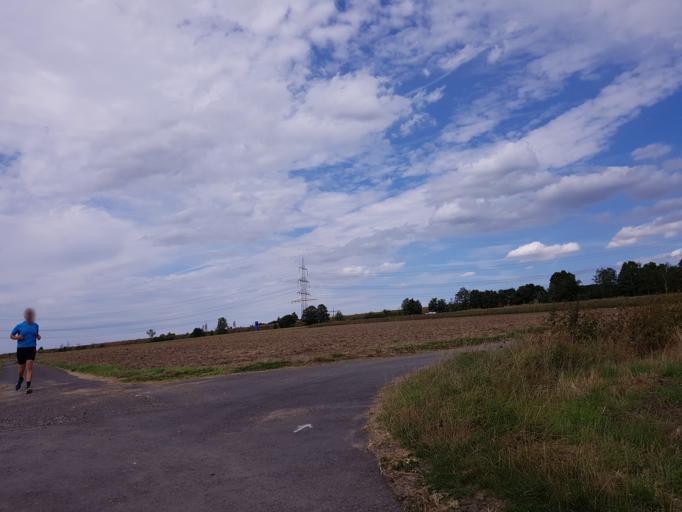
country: DE
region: Hesse
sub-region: Regierungsbezirk Giessen
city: Langgons
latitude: 50.5152
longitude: 8.6619
